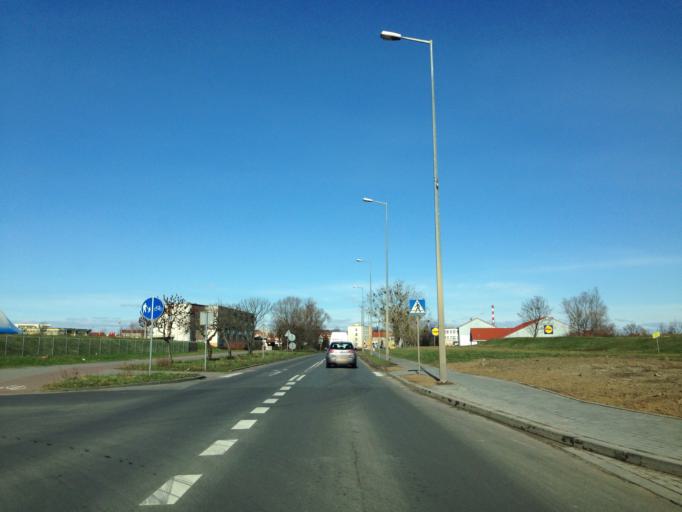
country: PL
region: Pomeranian Voivodeship
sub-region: Powiat malborski
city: Malbork
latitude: 54.0260
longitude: 19.0476
